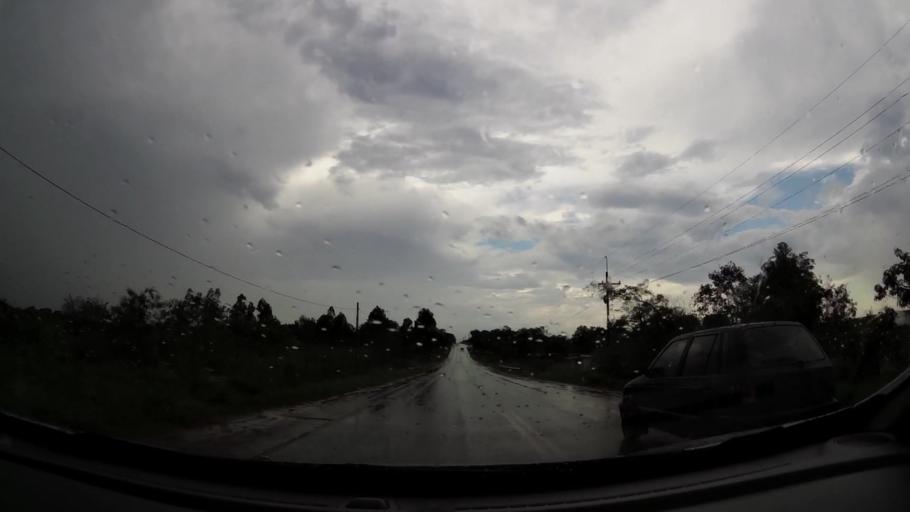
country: PY
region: Alto Parana
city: Presidente Franco
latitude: -25.5636
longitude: -54.6658
